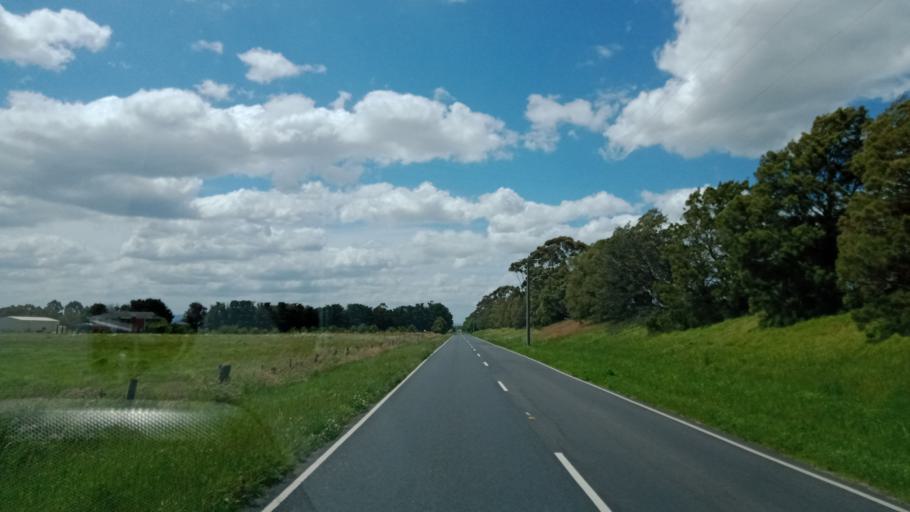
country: AU
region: Victoria
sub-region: Kingston
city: Patterson Lakes
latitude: -38.0500
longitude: 145.1610
